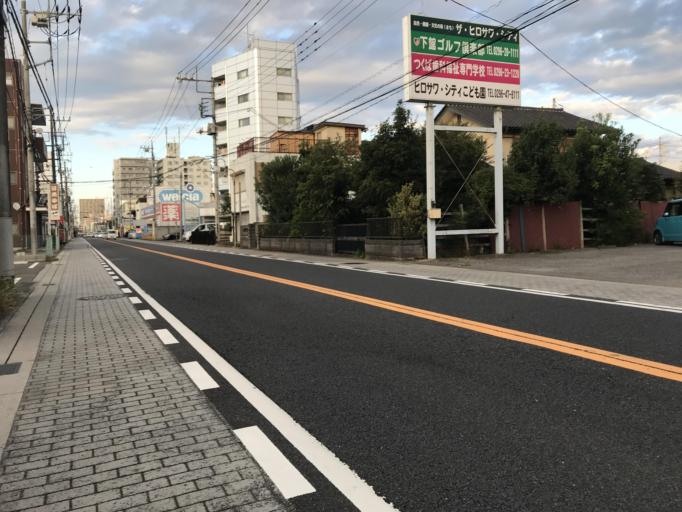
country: JP
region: Tochigi
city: Oyama
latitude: 36.3054
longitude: 139.7995
